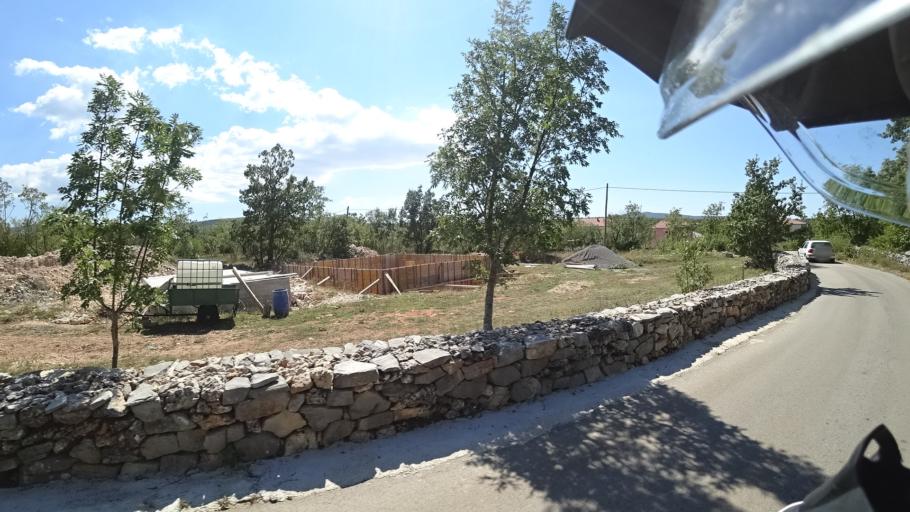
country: HR
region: Splitsko-Dalmatinska
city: Hrvace
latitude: 43.7432
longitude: 16.4391
